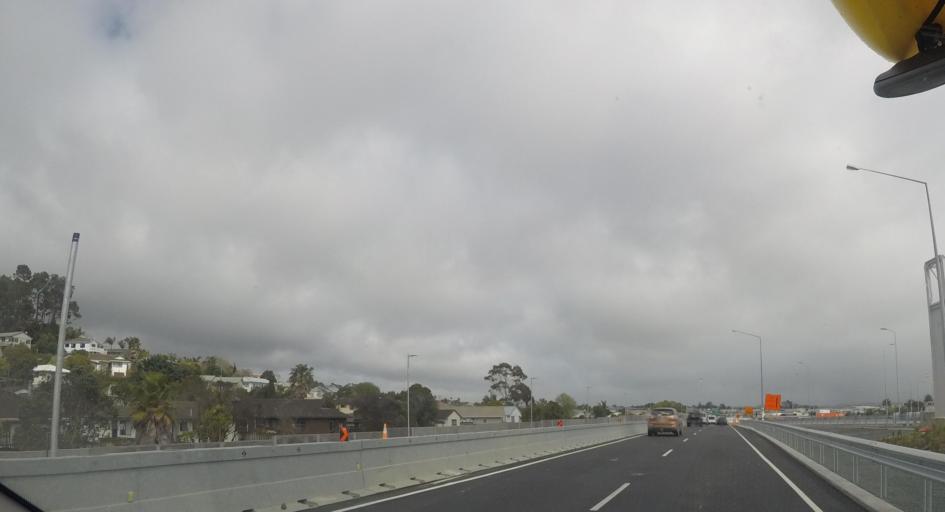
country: NZ
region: Auckland
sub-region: Auckland
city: Rothesay Bay
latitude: -36.7524
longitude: 174.7188
